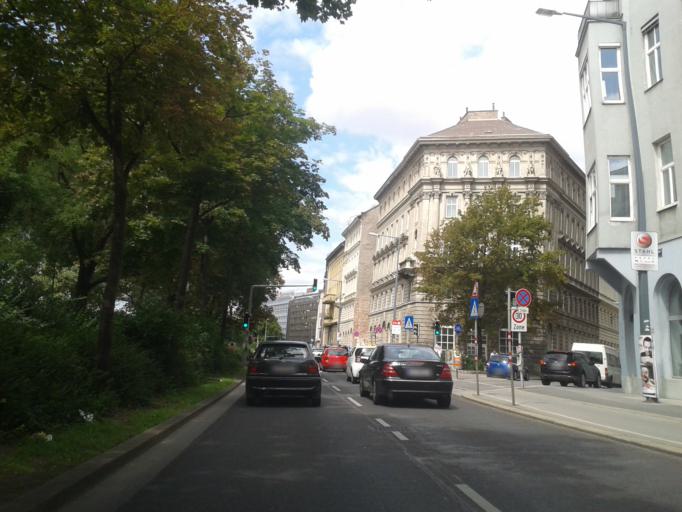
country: AT
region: Vienna
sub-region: Wien Stadt
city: Vienna
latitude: 48.2159
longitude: 16.3748
